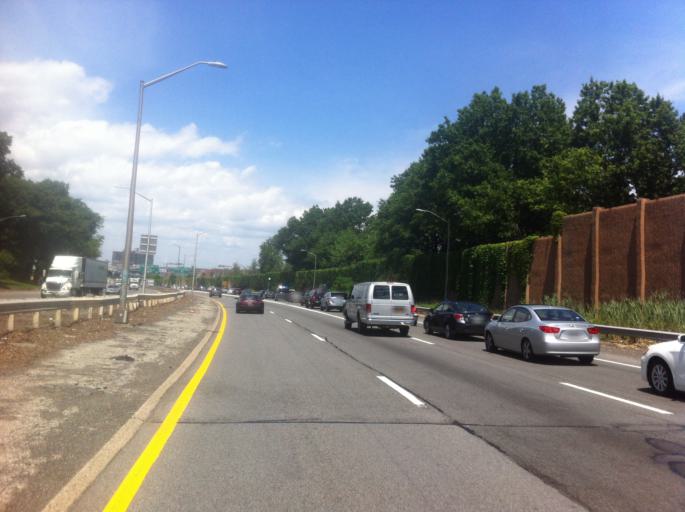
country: US
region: New York
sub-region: Nassau County
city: East Atlantic Beach
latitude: 40.7771
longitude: -73.7846
